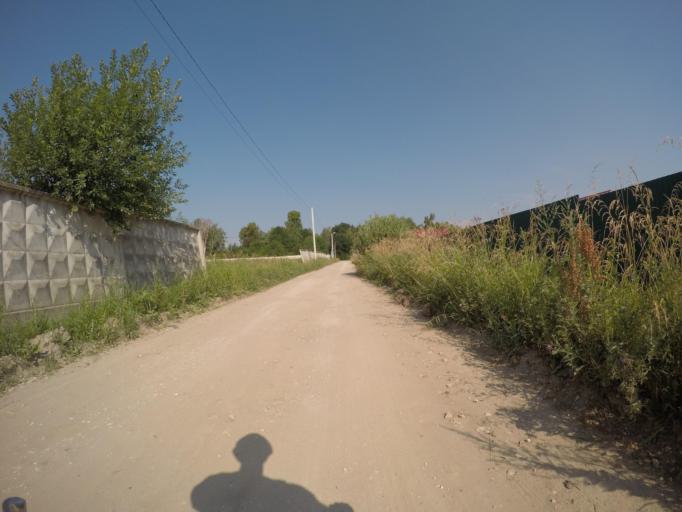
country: RU
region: Moskovskaya
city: Rechitsy
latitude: 55.6125
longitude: 38.5201
